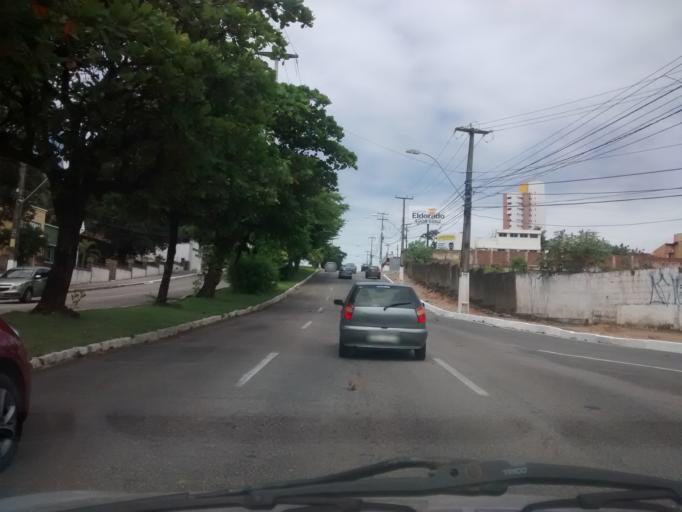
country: BR
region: Rio Grande do Norte
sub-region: Natal
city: Natal
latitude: -5.7960
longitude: -35.2044
